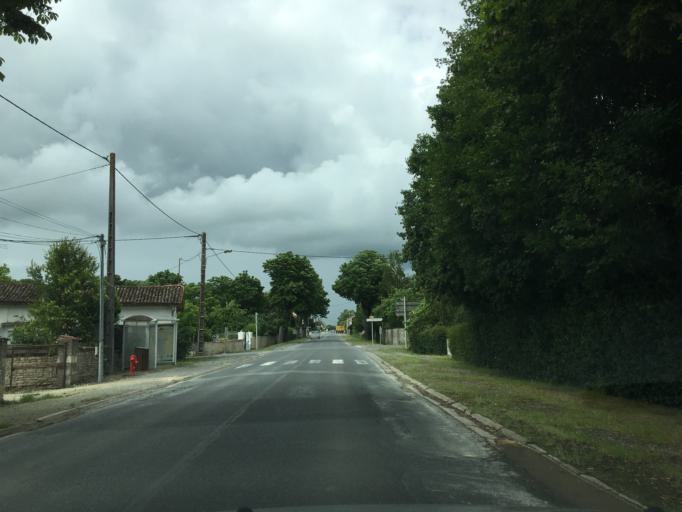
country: FR
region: Poitou-Charentes
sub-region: Departement des Deux-Sevres
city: Beauvoir-sur-Niort
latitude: 46.0945
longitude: -0.5032
